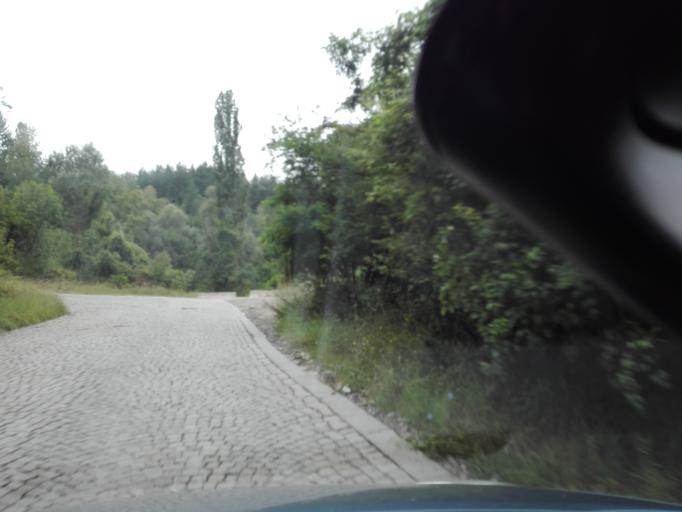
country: BG
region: Sofia-Capital
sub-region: Stolichna Obshtina
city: Sofia
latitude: 42.6058
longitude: 23.3939
